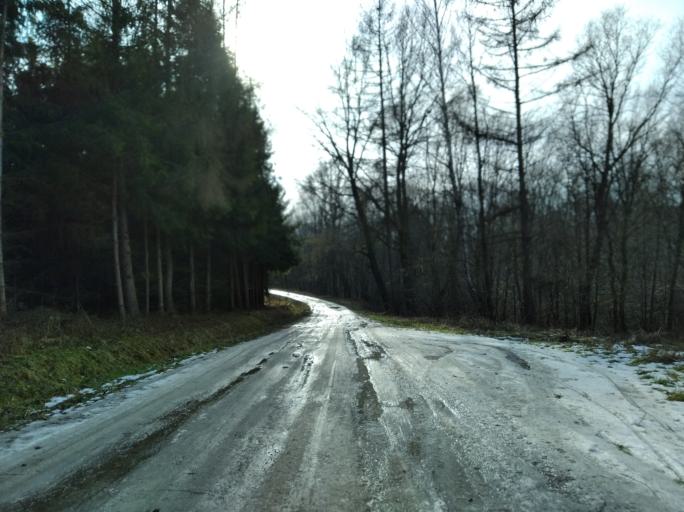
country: PL
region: Subcarpathian Voivodeship
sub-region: Powiat brzozowski
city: Grabownica Starzenska
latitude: 49.6443
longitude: 22.0650
